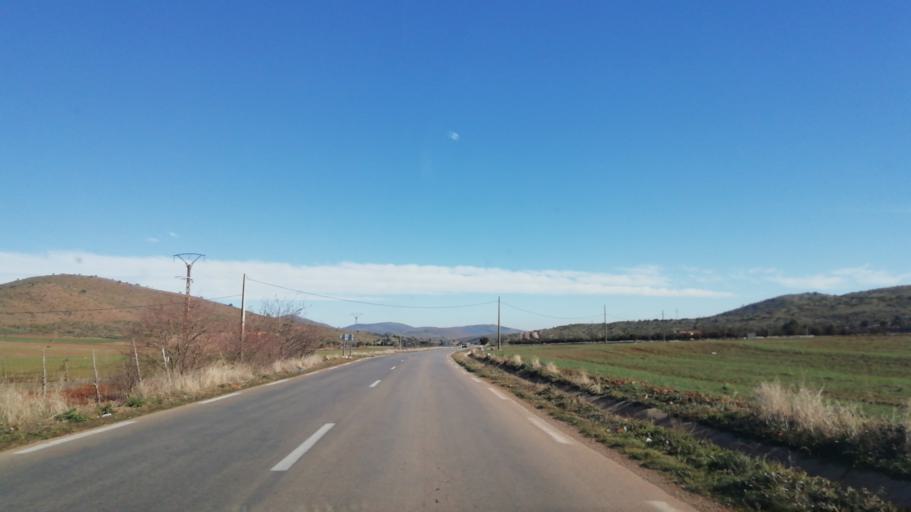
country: DZ
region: Tlemcen
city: Sebdou
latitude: 34.7445
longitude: -1.1652
